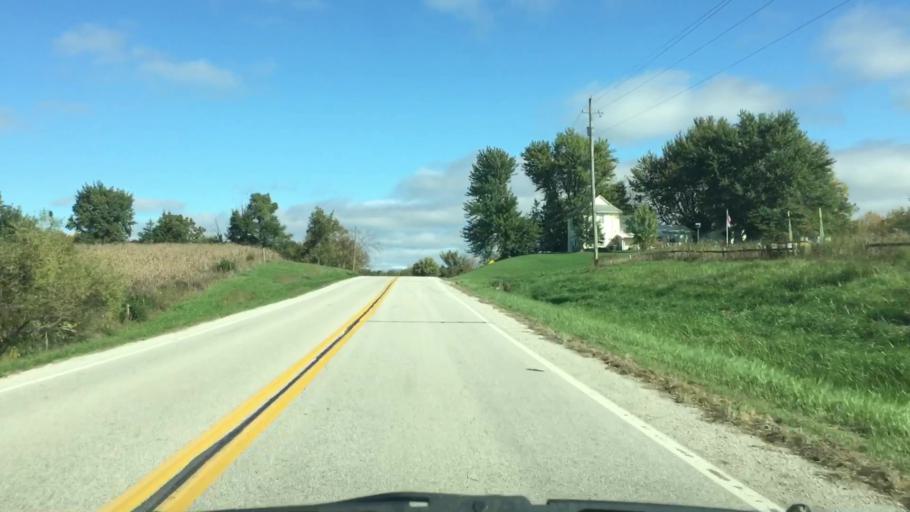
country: US
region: Iowa
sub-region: Decatur County
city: Leon
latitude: 40.6956
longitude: -93.7743
